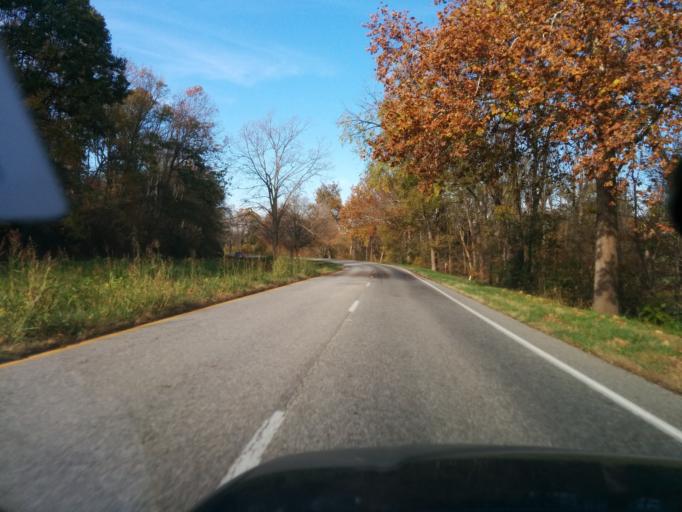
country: US
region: Virginia
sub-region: Rockbridge County
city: East Lexington
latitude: 37.8492
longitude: -79.3440
